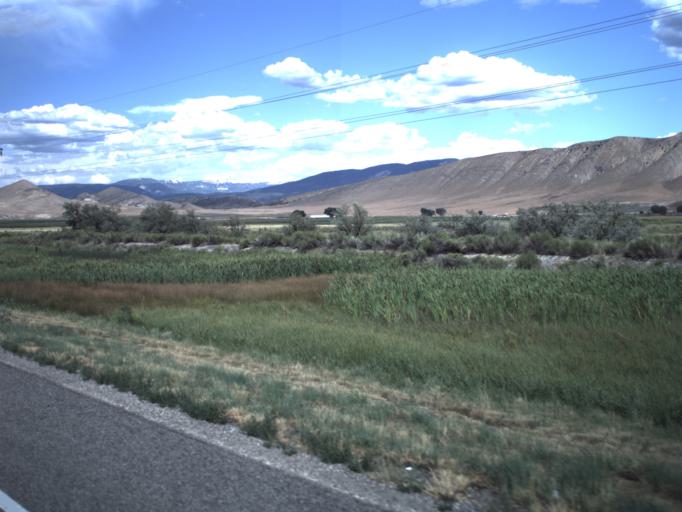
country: US
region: Utah
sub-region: Sevier County
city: Salina
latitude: 38.9881
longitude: -111.8490
